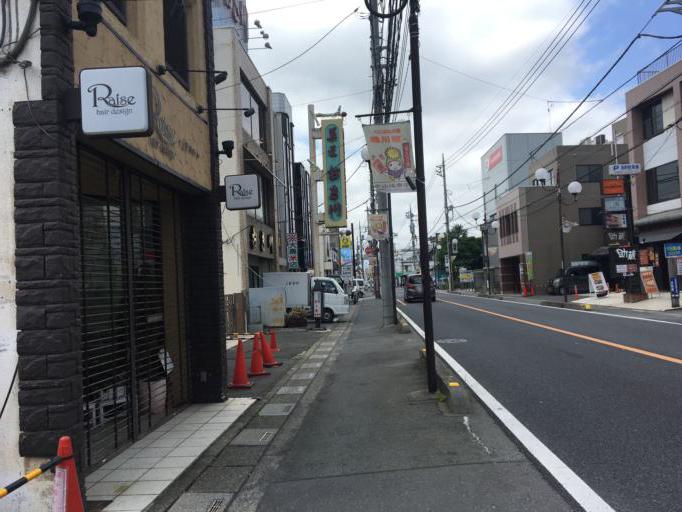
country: JP
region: Saitama
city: Okegawa
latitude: 36.0005
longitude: 139.5660
